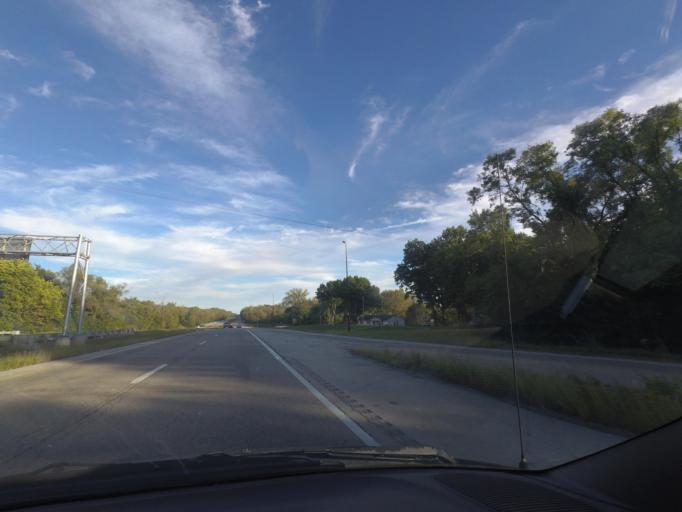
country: US
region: Illinois
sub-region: Sangamon County
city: Grandview
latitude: 39.7846
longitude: -89.5968
